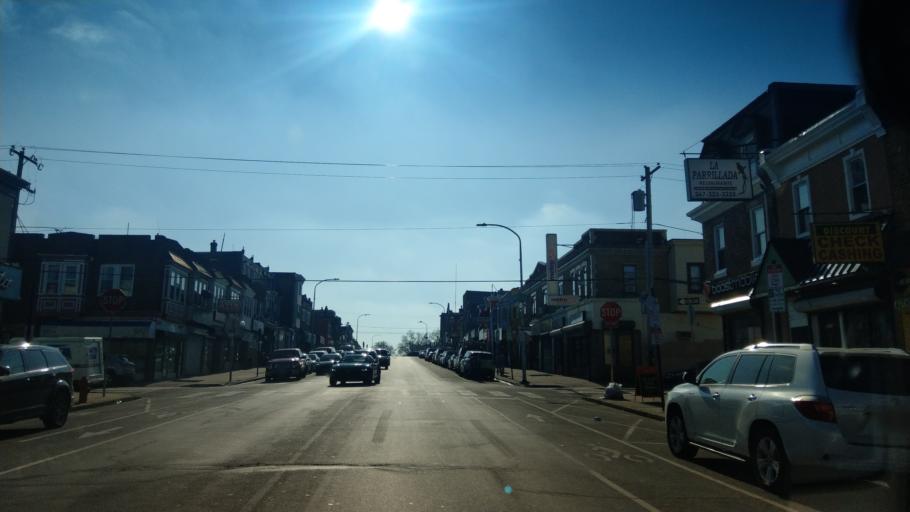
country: US
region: Pennsylvania
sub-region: Montgomery County
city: Rockledge
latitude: 40.0276
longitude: -75.1325
